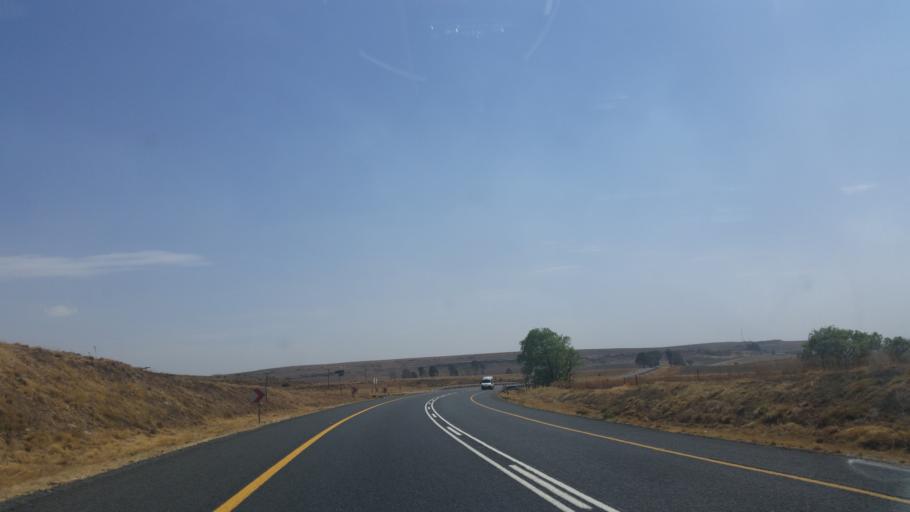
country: ZA
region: Orange Free State
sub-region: Thabo Mofutsanyana District Municipality
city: Bethlehem
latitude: -28.3098
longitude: 28.4946
